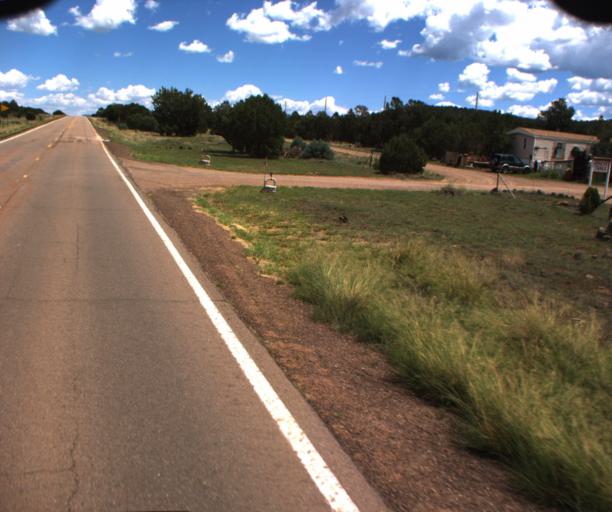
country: US
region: Arizona
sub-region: Navajo County
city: Pinetop-Lakeside
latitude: 34.2739
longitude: -109.7657
